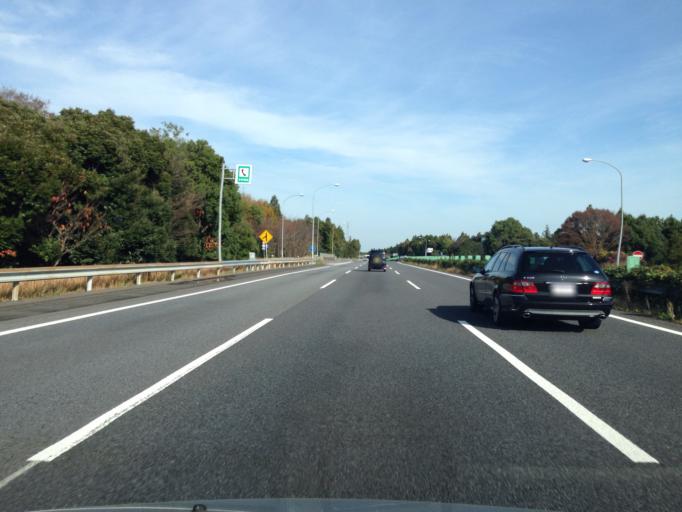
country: JP
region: Ibaraki
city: Tomobe
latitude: 36.2813
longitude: 140.3179
